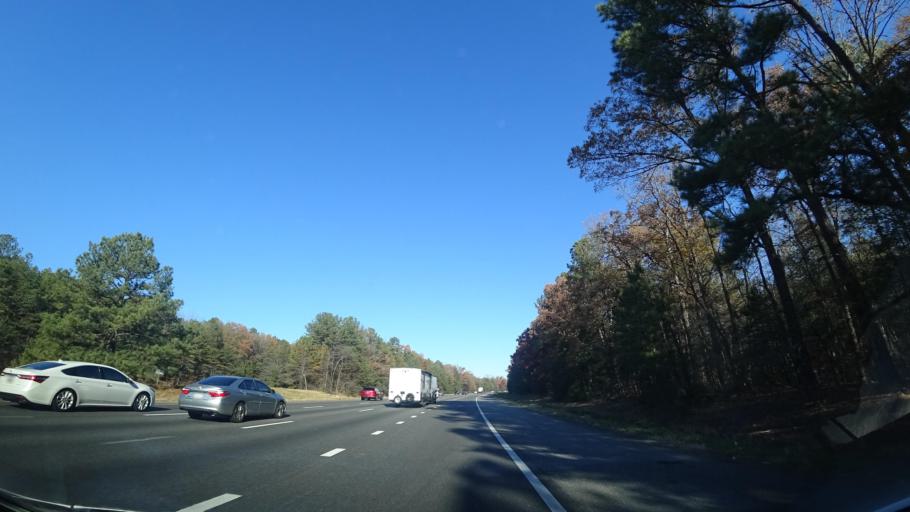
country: US
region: Virginia
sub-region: Hanover County
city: Ashland
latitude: 37.8486
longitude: -77.4525
